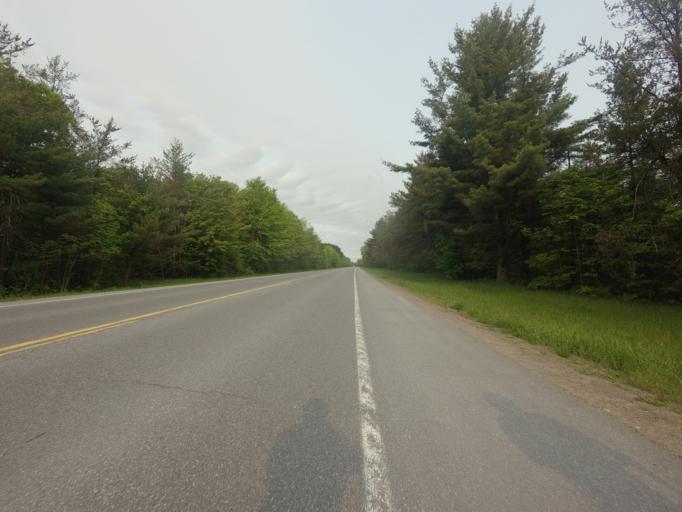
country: US
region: New York
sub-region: Jefferson County
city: Carthage
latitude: 44.0330
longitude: -75.6014
